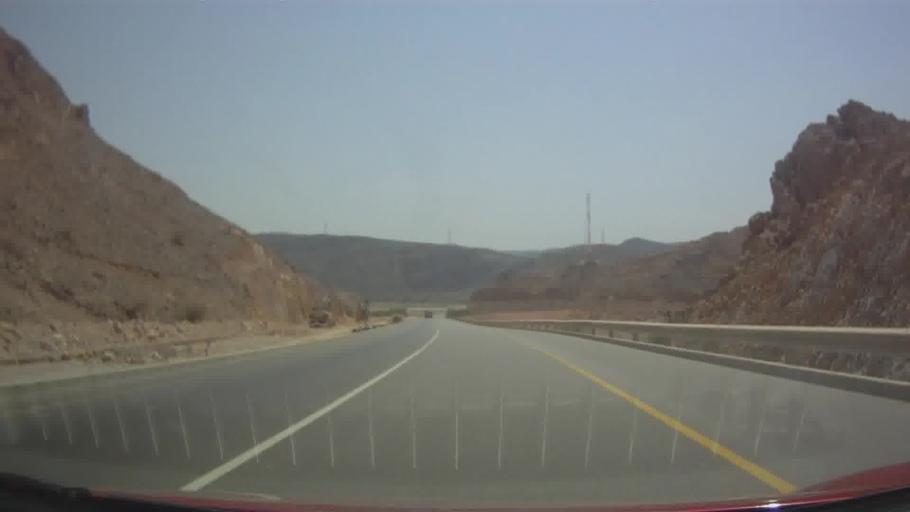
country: OM
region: Muhafazat Masqat
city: Muscat
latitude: 23.5182
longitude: 58.6331
